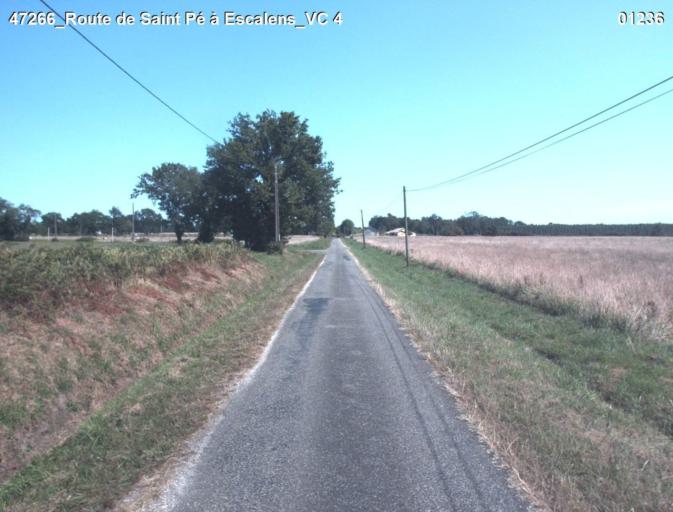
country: FR
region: Aquitaine
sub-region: Departement des Landes
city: Gabarret
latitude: 44.0011
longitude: 0.0753
